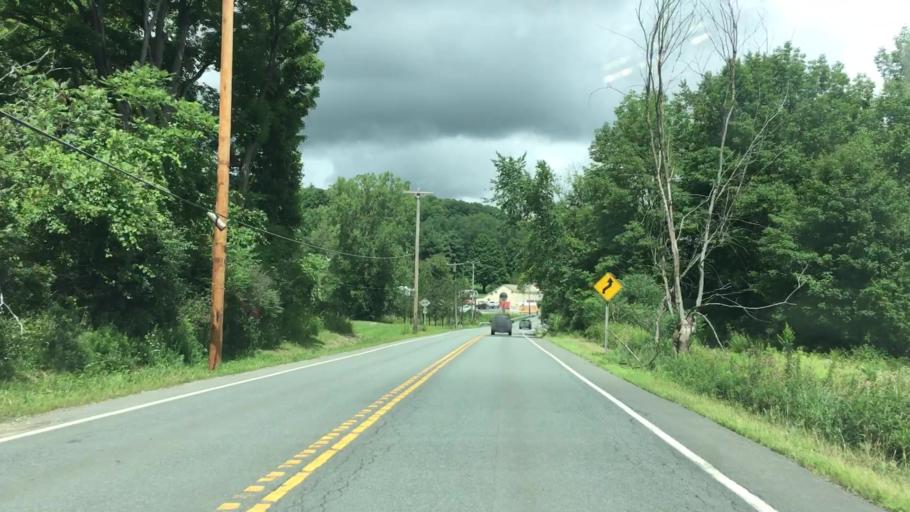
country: US
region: New York
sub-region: Rensselaer County
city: Hoosick Falls
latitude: 42.8703
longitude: -73.3109
